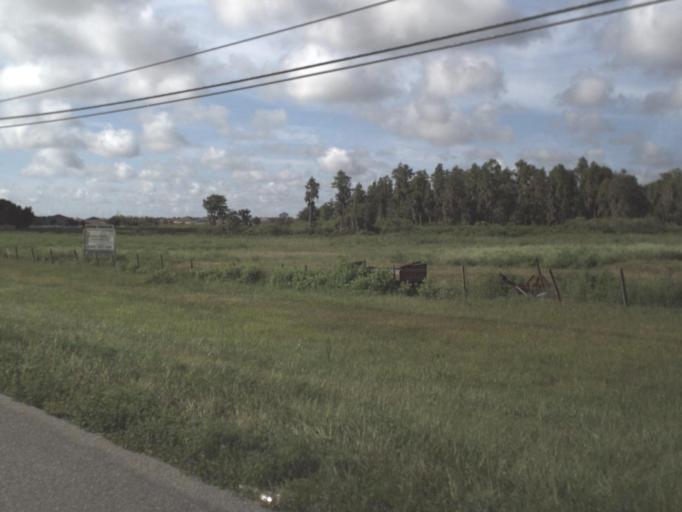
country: US
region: Florida
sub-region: Pasco County
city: Land O' Lakes
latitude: 28.3095
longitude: -82.5037
